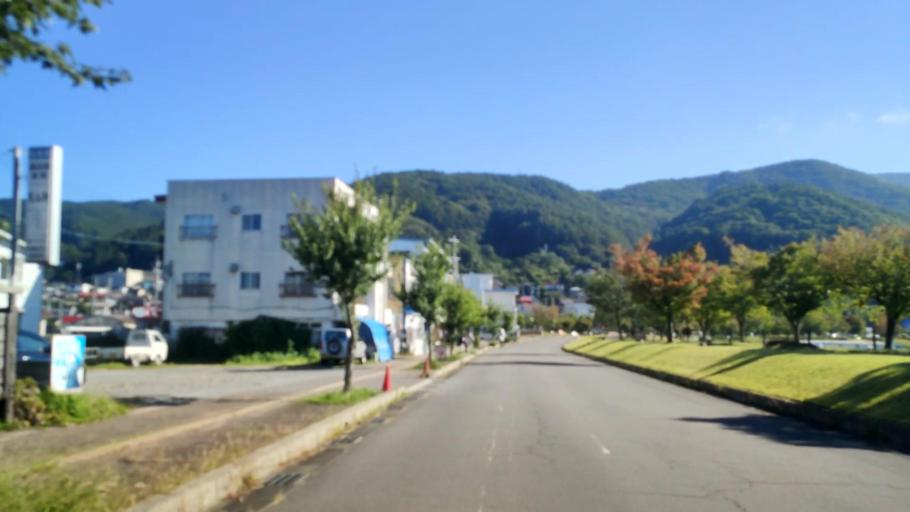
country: JP
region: Nagano
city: Suwa
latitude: 36.0664
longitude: 138.0947
